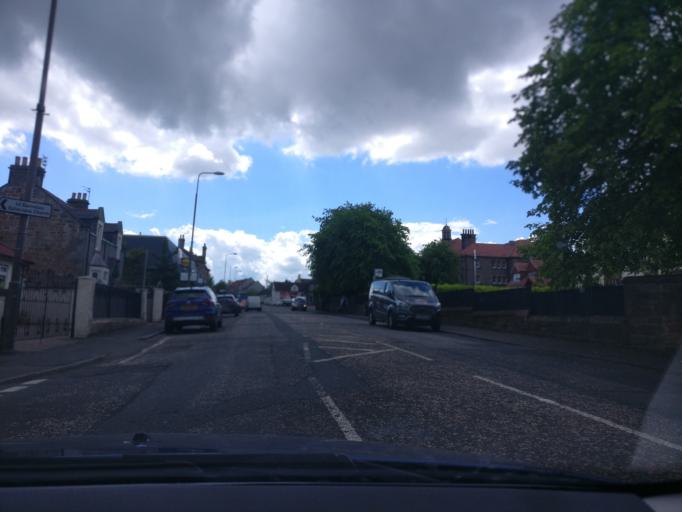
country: GB
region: Scotland
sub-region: Midlothian
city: Loanhead
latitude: 55.9070
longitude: -3.1345
